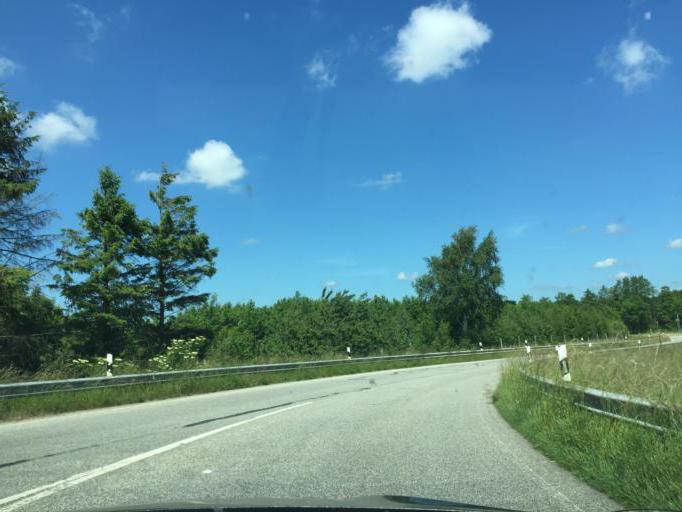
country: DE
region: Schleswig-Holstein
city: Harrislee
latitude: 54.7786
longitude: 9.3785
